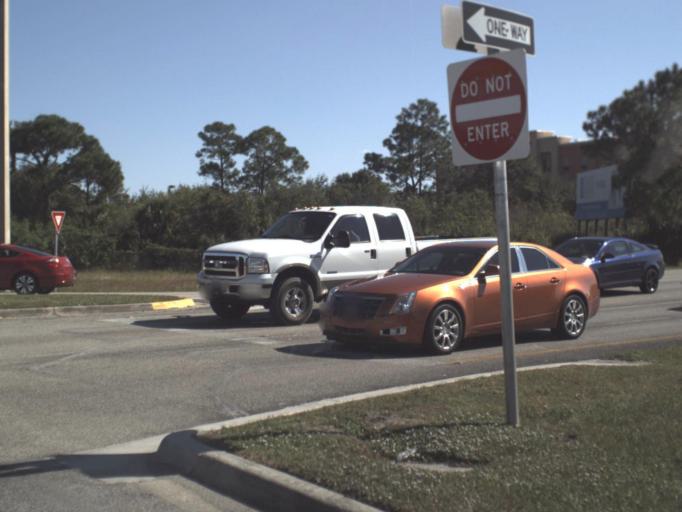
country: US
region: Florida
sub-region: Brevard County
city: South Patrick Shores
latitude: 28.2302
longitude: -80.7177
